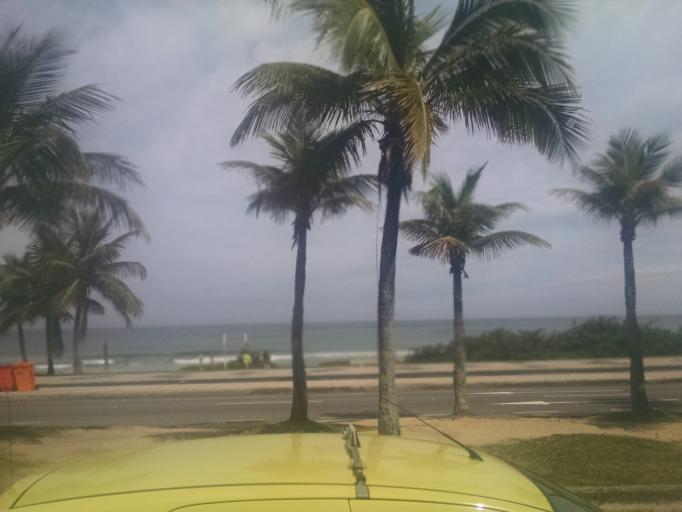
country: BR
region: Rio de Janeiro
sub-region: Rio De Janeiro
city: Rio de Janeiro
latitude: -23.0126
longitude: -43.3198
